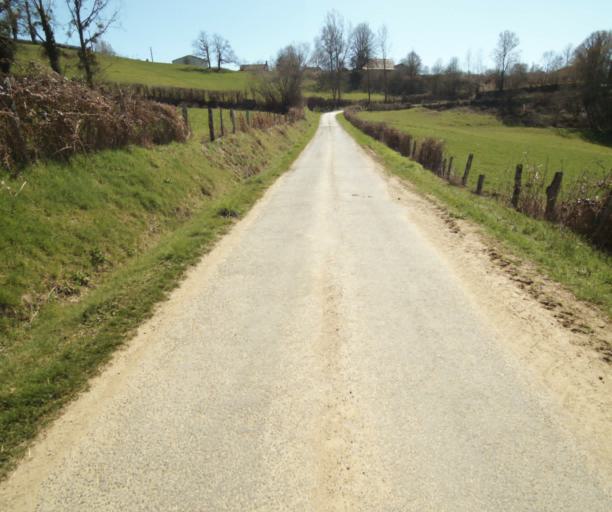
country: FR
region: Limousin
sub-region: Departement de la Correze
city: Chamboulive
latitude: 45.4492
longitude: 1.6738
